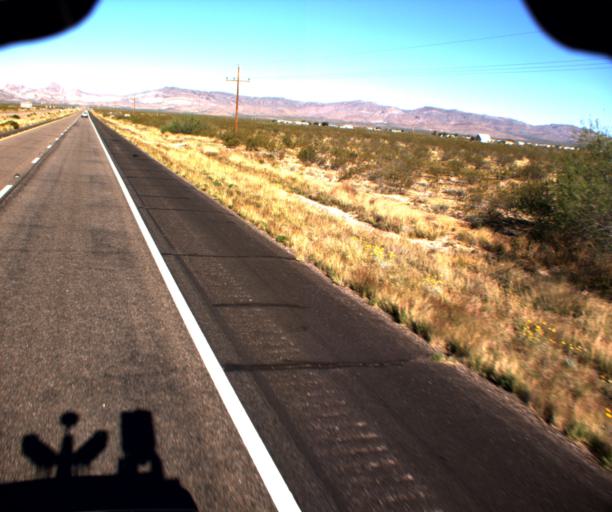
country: US
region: Arizona
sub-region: Mohave County
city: Golden Valley
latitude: 35.2260
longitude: -114.2957
